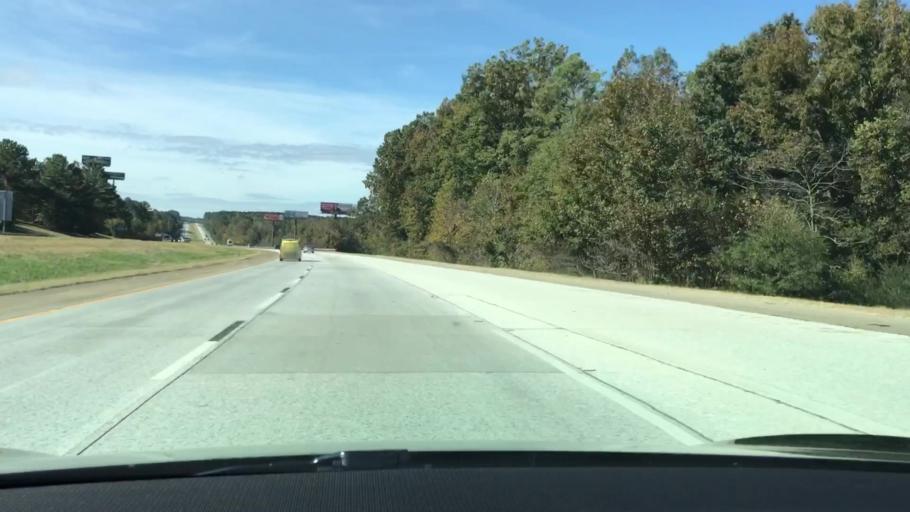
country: US
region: Georgia
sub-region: Greene County
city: Greensboro
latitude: 33.5458
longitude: -83.2127
